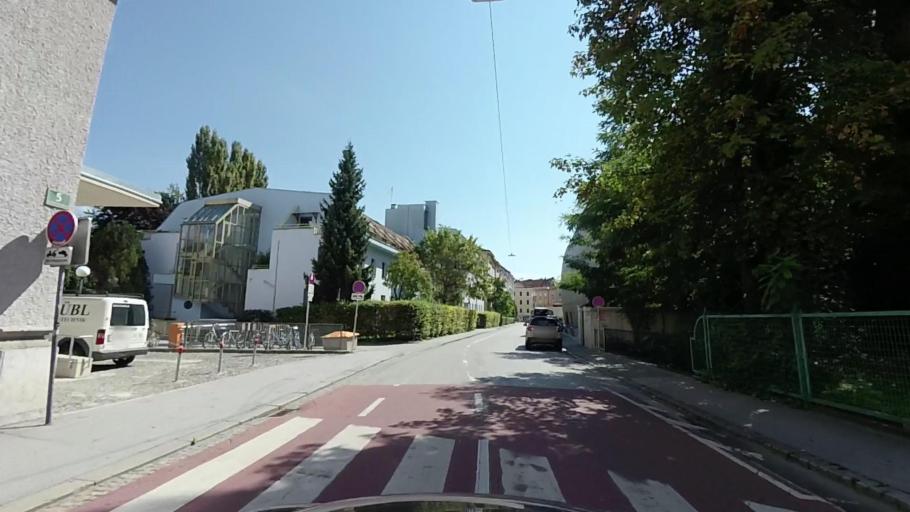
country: AT
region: Styria
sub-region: Graz Stadt
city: Graz
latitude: 47.0738
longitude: 15.4504
